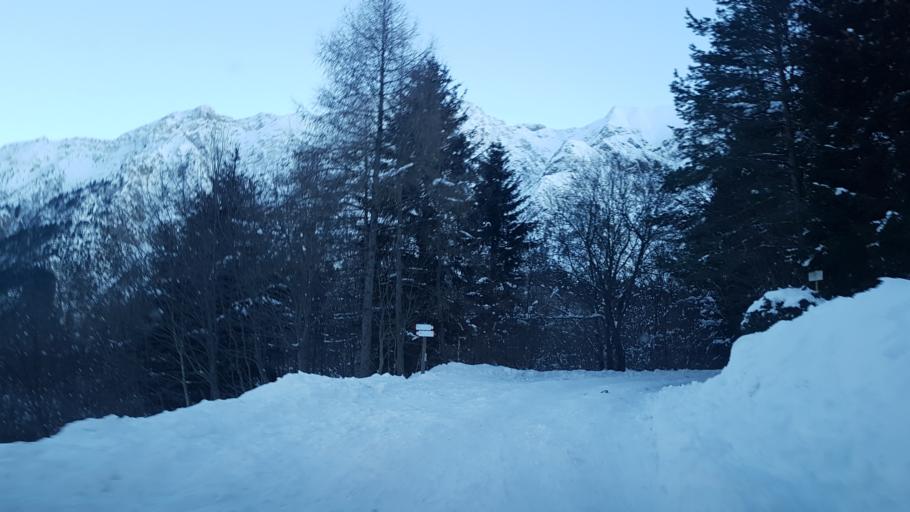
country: IT
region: Friuli Venezia Giulia
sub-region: Provincia di Udine
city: Isola
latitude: 46.2811
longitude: 13.1671
